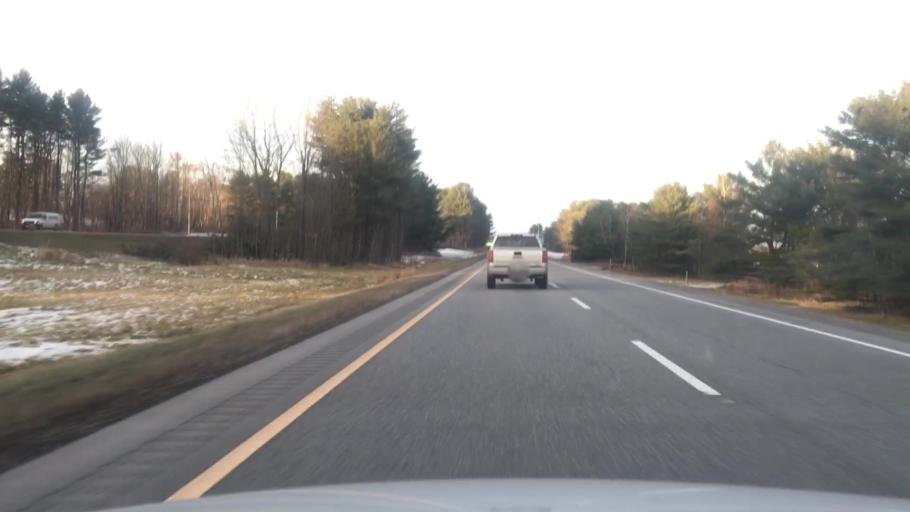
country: US
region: Maine
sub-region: Kennebec County
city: Oakland
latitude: 44.5005
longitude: -69.7039
